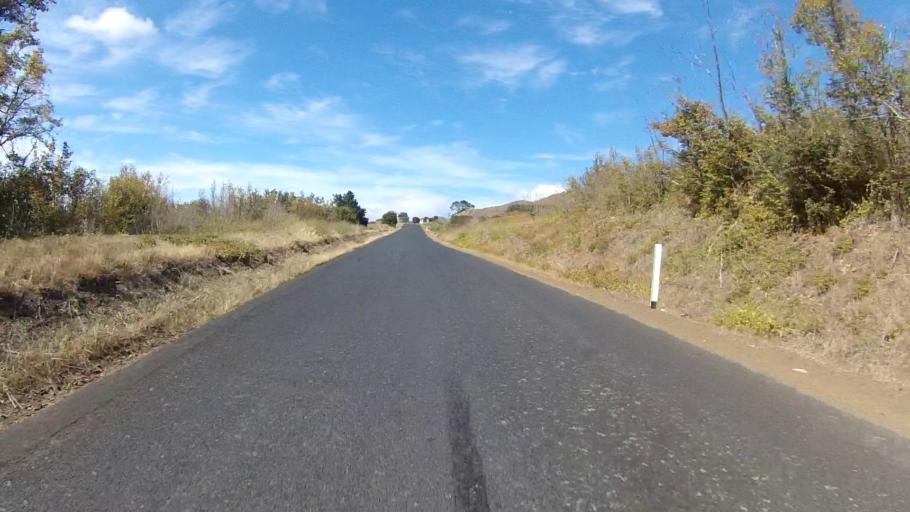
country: AU
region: Tasmania
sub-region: Brighton
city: Bridgewater
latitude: -42.7332
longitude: 147.2604
